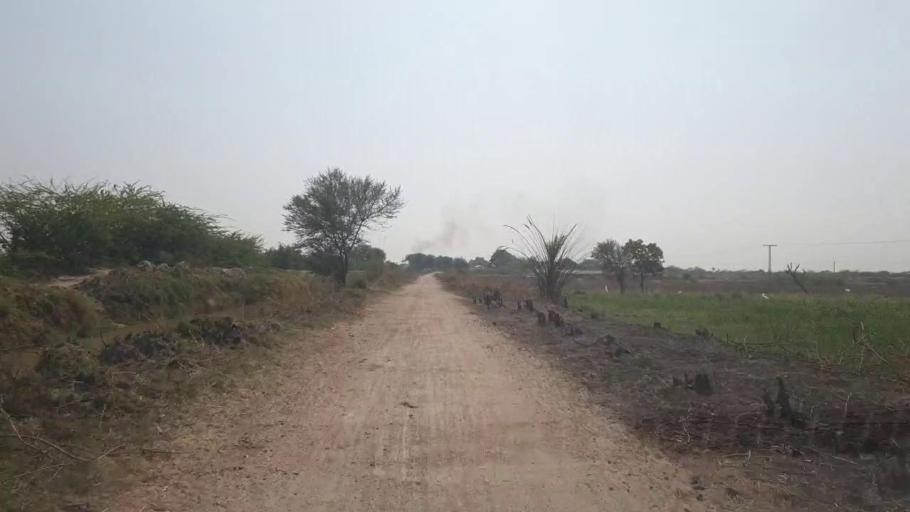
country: PK
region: Sindh
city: Dhoro Naro
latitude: 25.5068
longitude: 69.5433
